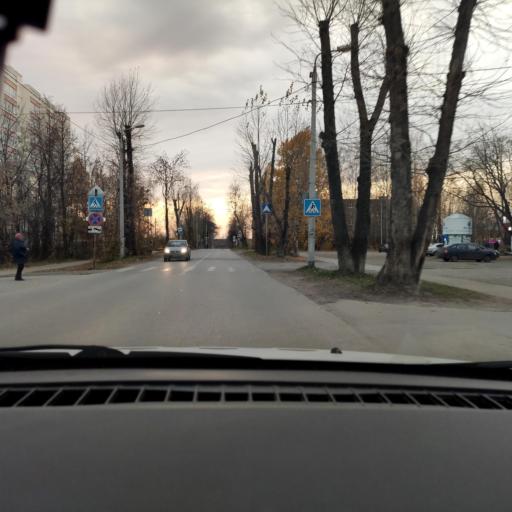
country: RU
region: Perm
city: Perm
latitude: 58.1202
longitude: 56.3844
